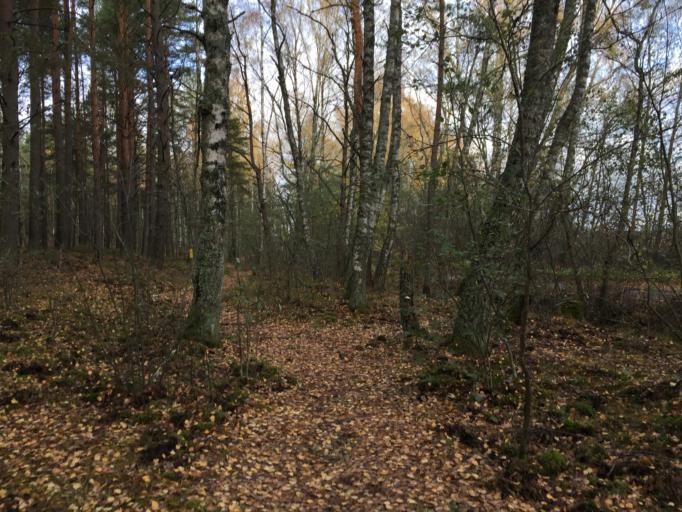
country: LV
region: Carnikava
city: Carnikava
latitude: 57.1459
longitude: 24.2636
